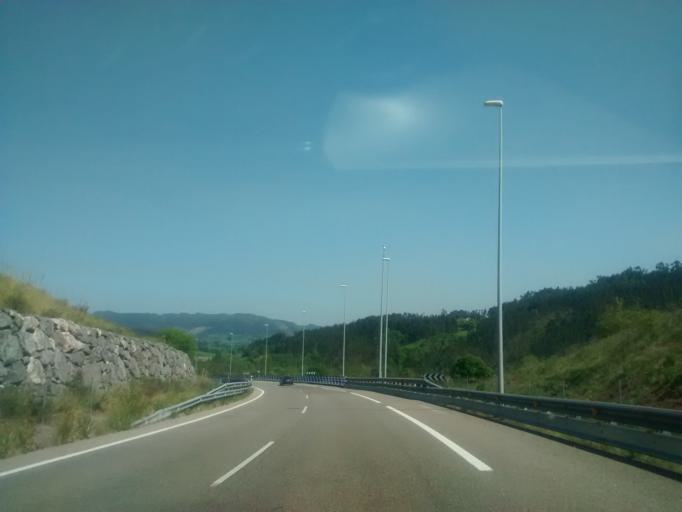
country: ES
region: Asturias
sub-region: Province of Asturias
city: Villaviciosa
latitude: 43.4644
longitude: -5.4893
